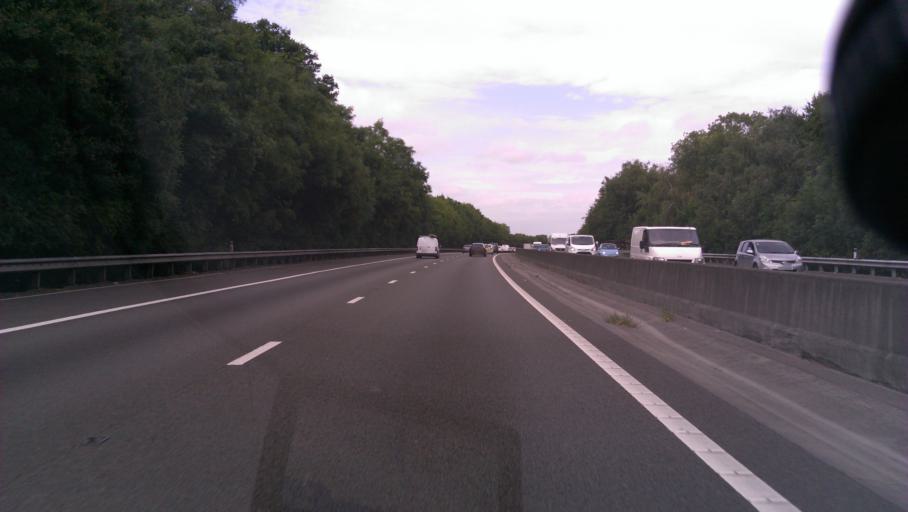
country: GB
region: England
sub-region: Essex
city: Elsenham
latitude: 51.9174
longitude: 0.2190
